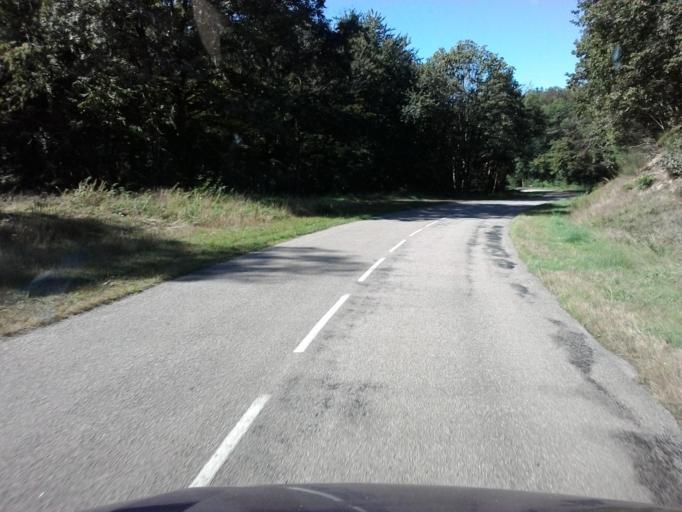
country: FR
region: Bourgogne
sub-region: Departement de la Nievre
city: Lormes
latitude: 47.2705
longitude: 3.8439
